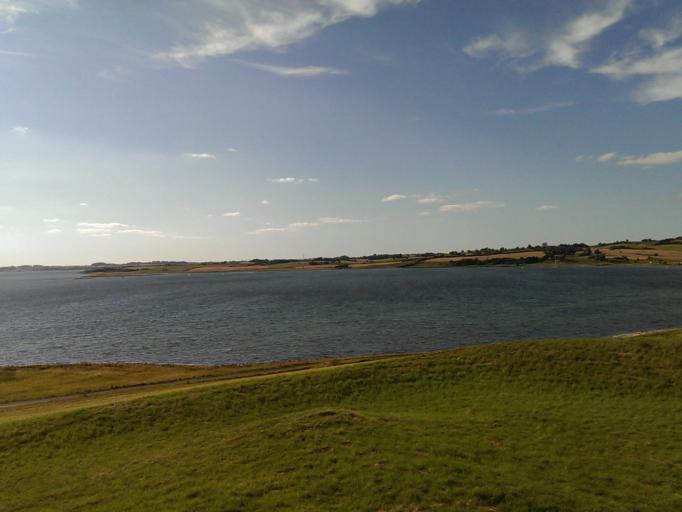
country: DK
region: Central Jutland
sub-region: Syddjurs Kommune
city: Ronde
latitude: 56.1623
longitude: 10.5300
